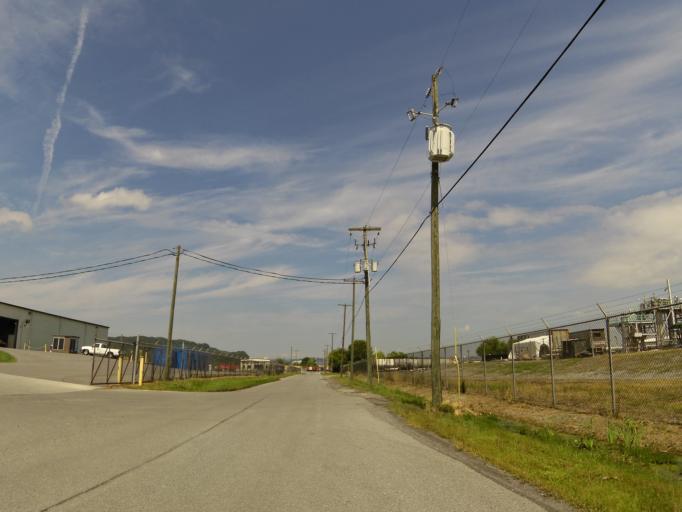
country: US
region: Tennessee
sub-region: Sullivan County
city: Kingsport
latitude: 36.5178
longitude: -82.5478
